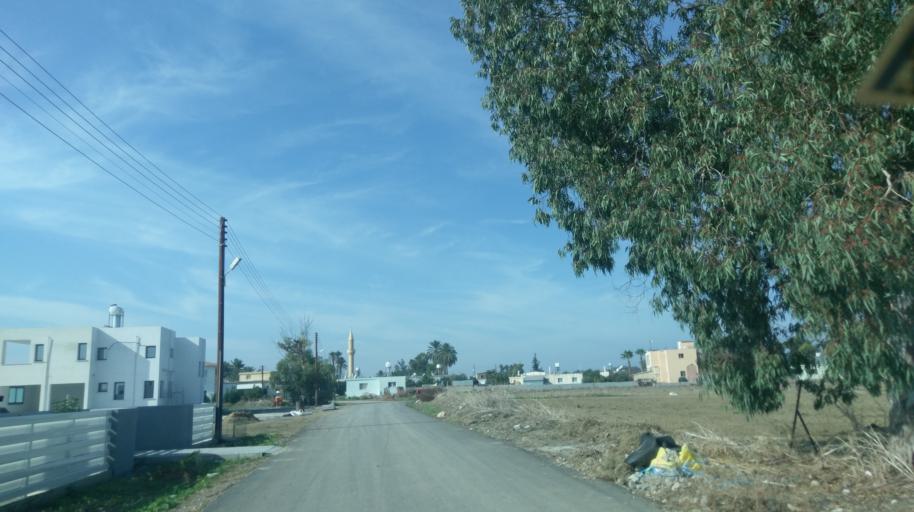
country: CY
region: Ammochostos
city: Lefkonoiko
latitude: 35.1676
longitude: 33.6424
